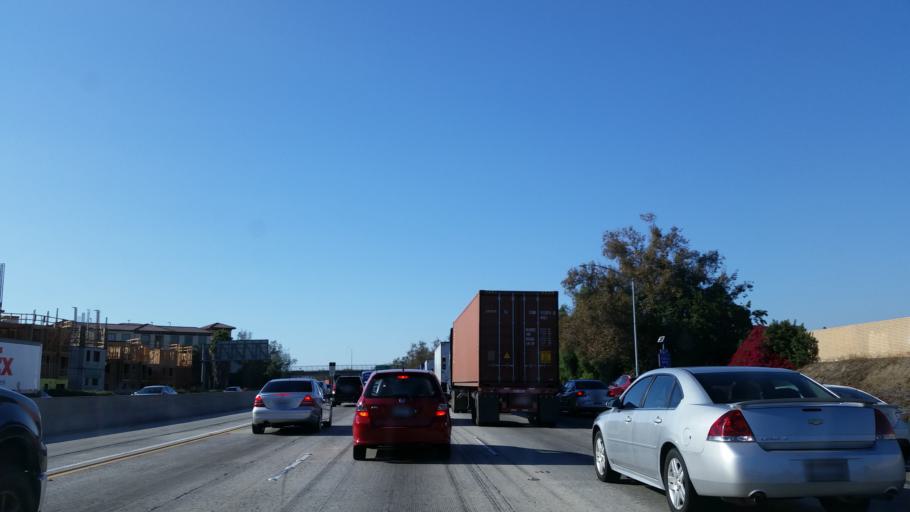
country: US
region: California
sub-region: Los Angeles County
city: Cerritos
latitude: 33.8738
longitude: -118.0609
